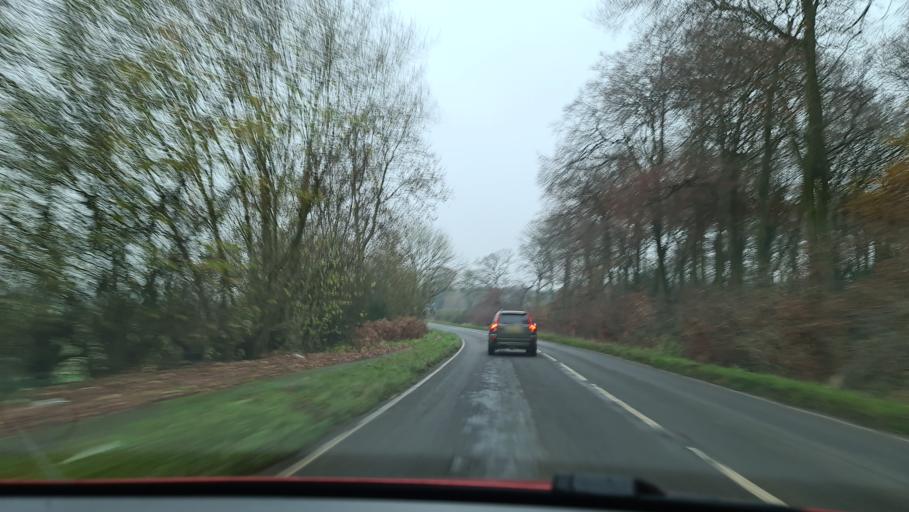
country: GB
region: England
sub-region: Buckinghamshire
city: Stokenchurch
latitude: 51.6529
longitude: -0.8729
